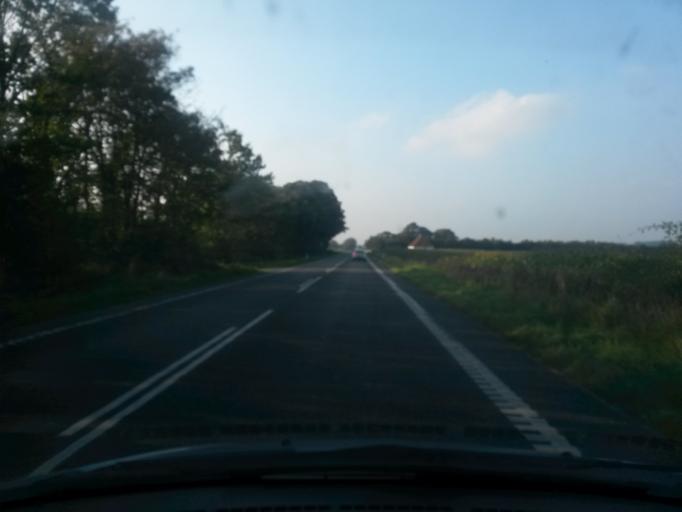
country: DK
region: Central Jutland
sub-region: Syddjurs Kommune
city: Hornslet
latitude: 56.3952
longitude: 10.2631
